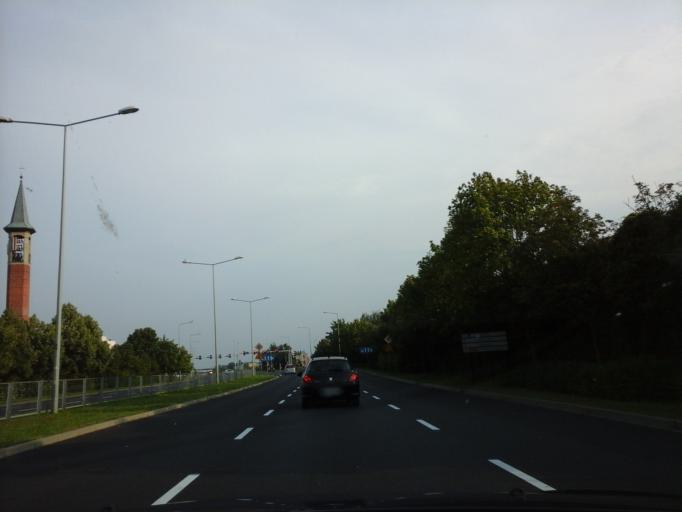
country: PL
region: Greater Poland Voivodeship
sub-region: Leszno
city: Leszno
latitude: 51.8486
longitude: 16.5913
